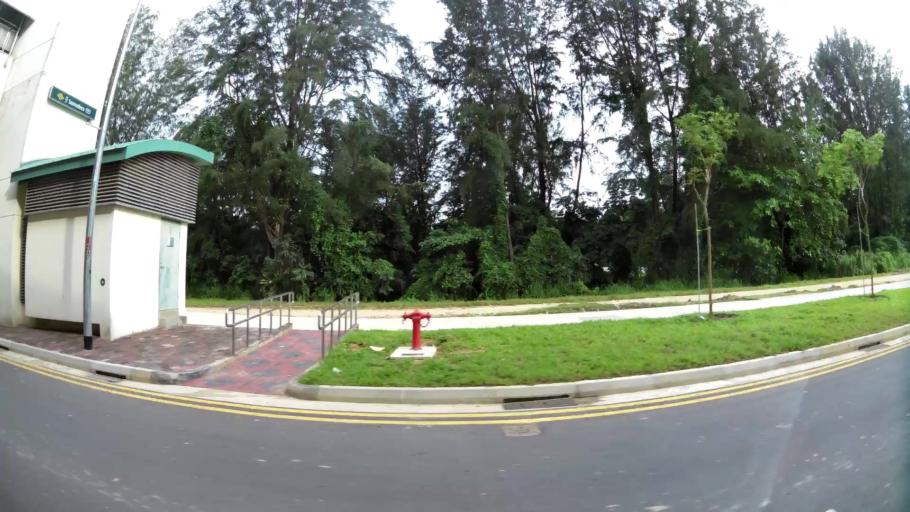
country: MY
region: Johor
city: Kampung Pasir Gudang Baru
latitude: 1.4156
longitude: 103.9021
